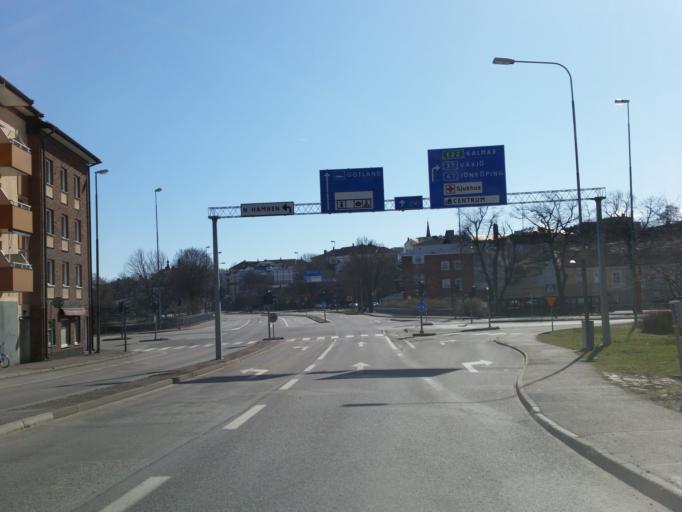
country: SE
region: Kalmar
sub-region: Oskarshamns Kommun
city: Oskarshamn
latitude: 57.2682
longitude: 16.4513
